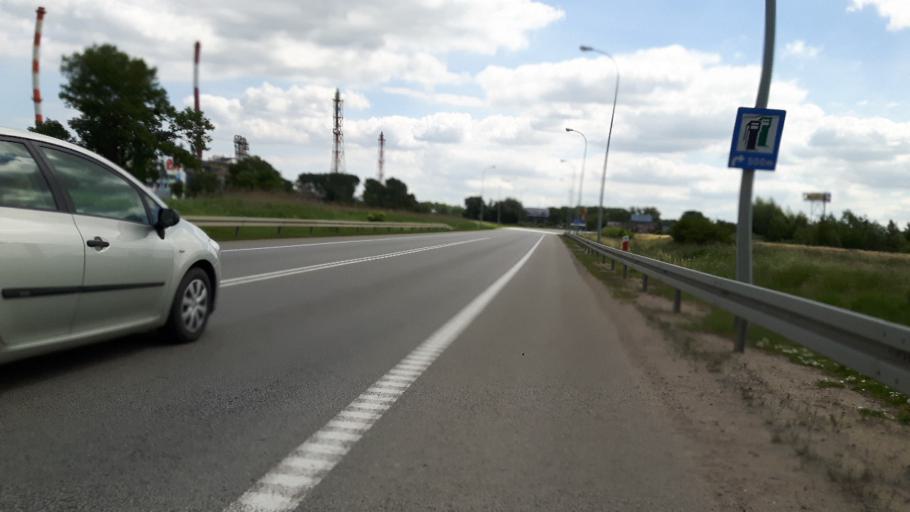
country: PL
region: Pomeranian Voivodeship
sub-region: Gdansk
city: Gdansk
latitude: 54.3405
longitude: 18.7306
